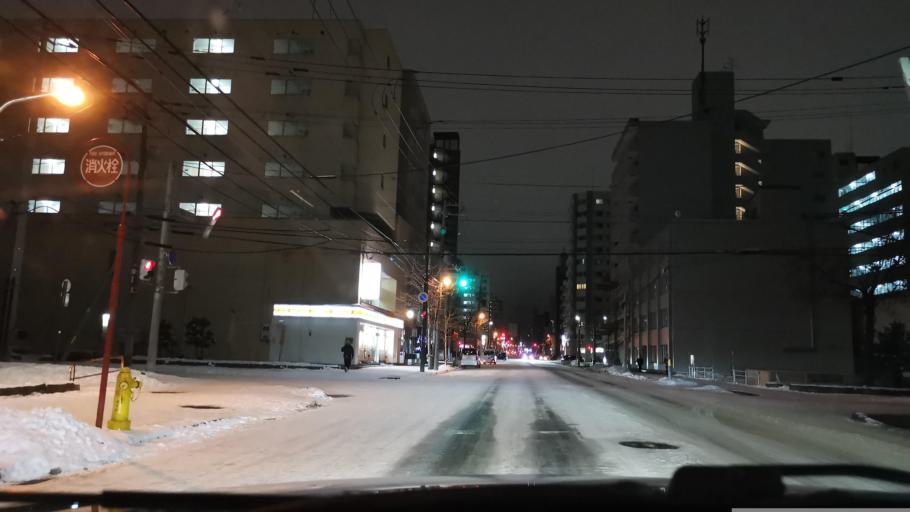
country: JP
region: Hokkaido
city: Sapporo
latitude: 43.0590
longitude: 141.3733
